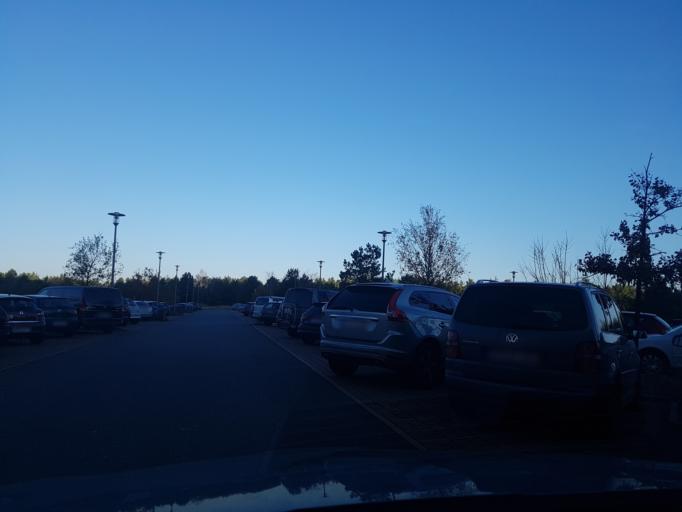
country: DE
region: Brandenburg
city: Halbe
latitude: 52.0406
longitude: 13.7475
